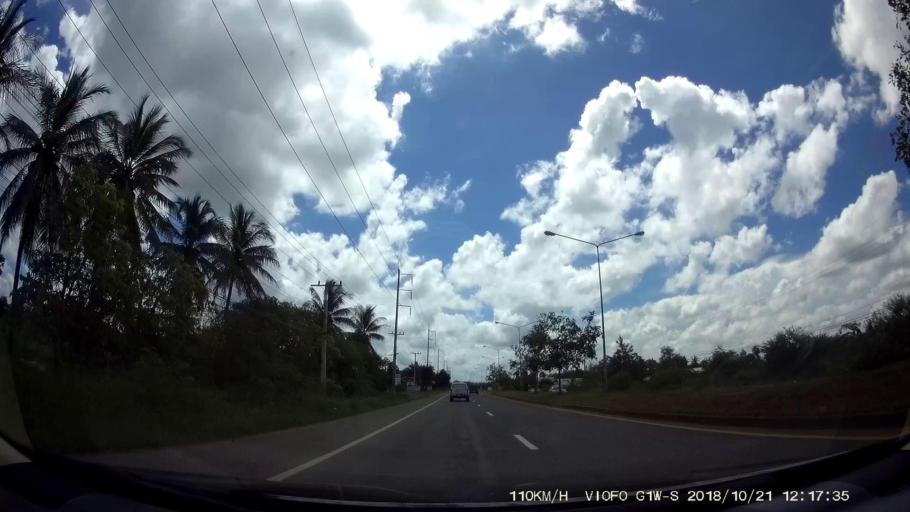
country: TH
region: Nakhon Ratchasima
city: Dan Khun Thot
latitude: 15.3298
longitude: 101.8197
